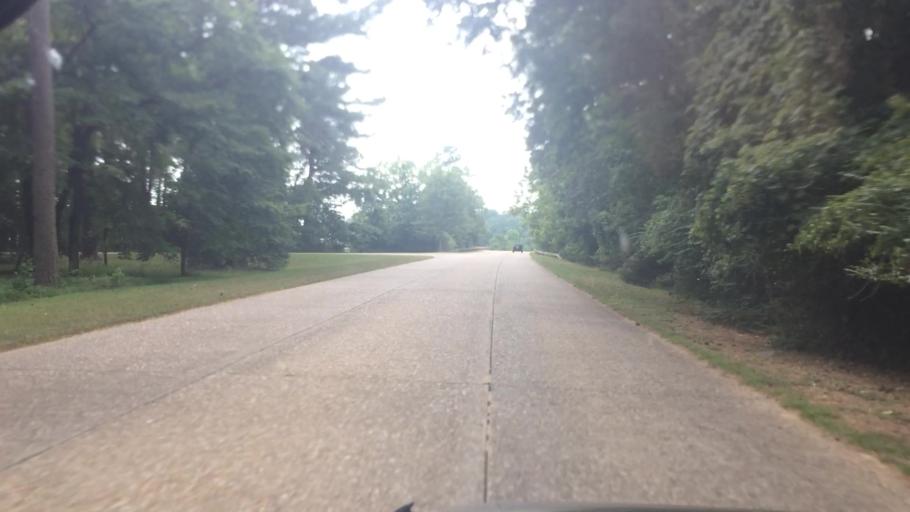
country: US
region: Virginia
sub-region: James City County
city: Williamsburg
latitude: 37.2144
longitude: -76.7420
